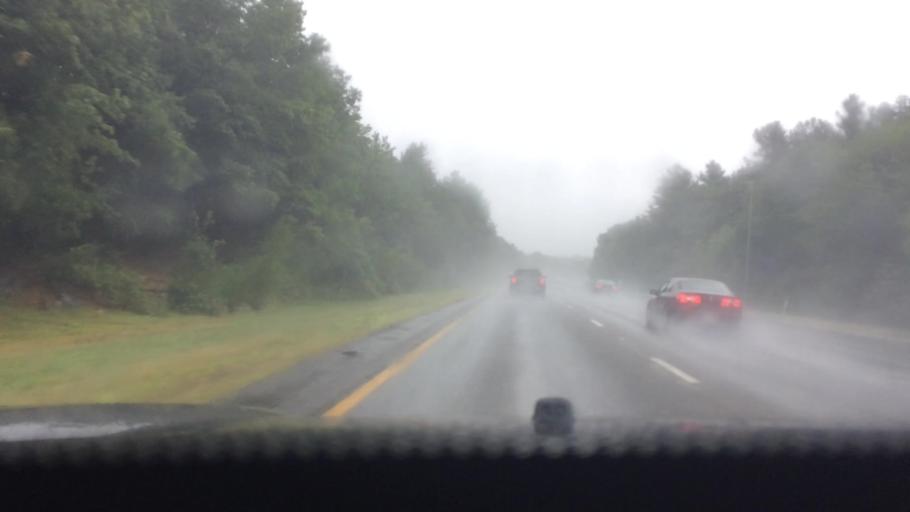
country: US
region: Massachusetts
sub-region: Worcester County
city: Harvard
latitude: 42.4904
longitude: -71.5421
